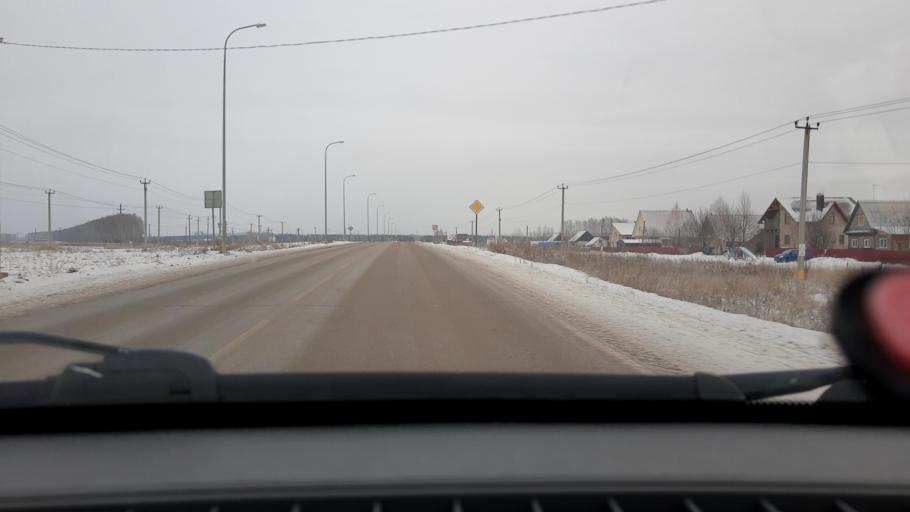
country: RU
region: Bashkortostan
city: Iglino
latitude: 54.8586
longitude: 56.4504
